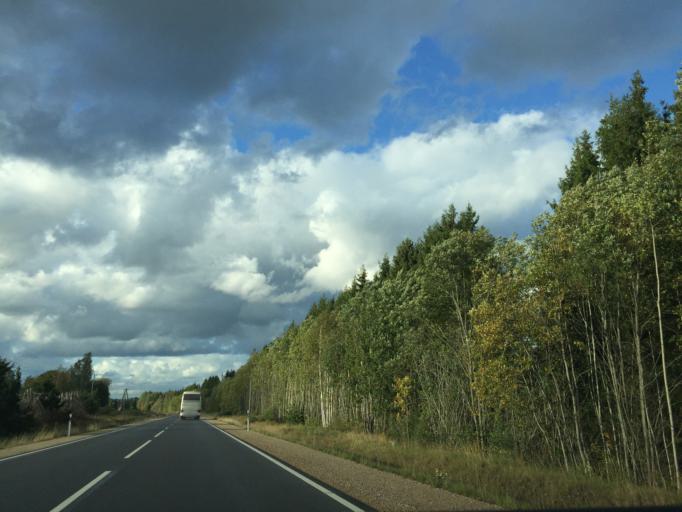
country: LV
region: Ligatne
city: Ligatne
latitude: 57.1411
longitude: 25.0805
